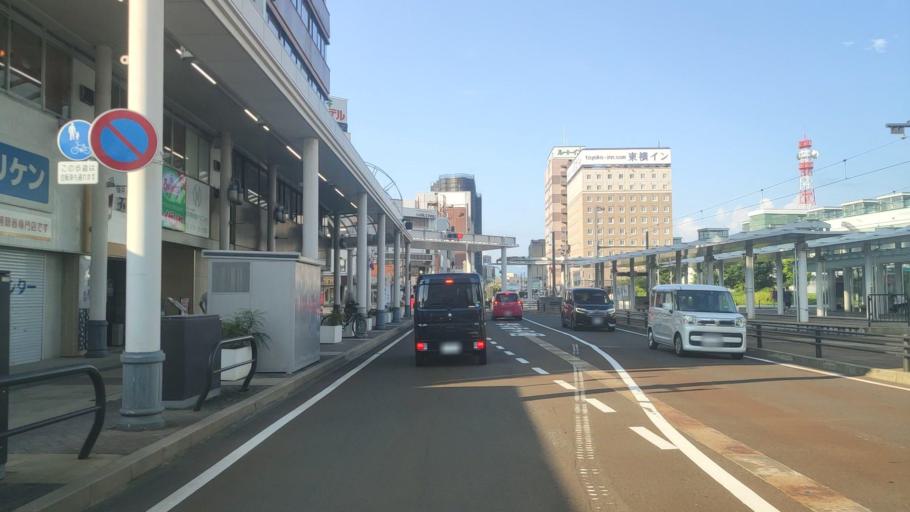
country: JP
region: Fukui
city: Fukui-shi
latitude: 36.0620
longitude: 136.2218
